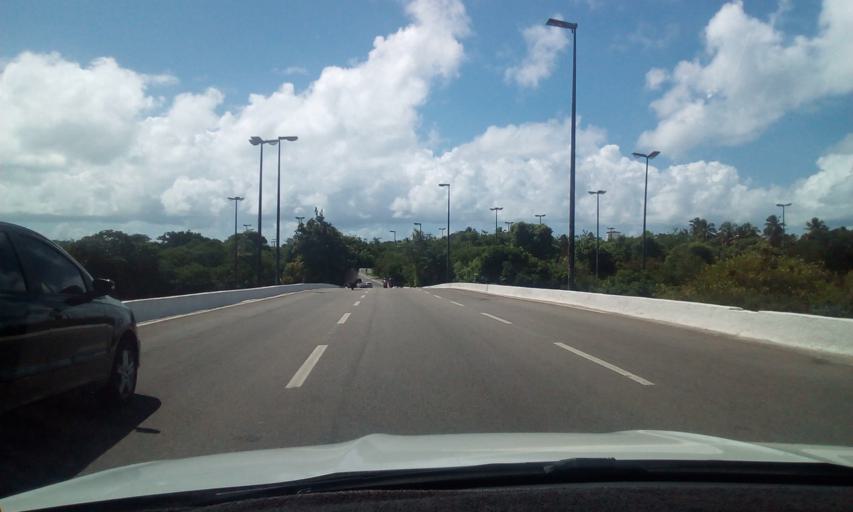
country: BR
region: Pernambuco
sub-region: Recife
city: Recife
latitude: -8.0362
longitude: -34.8708
